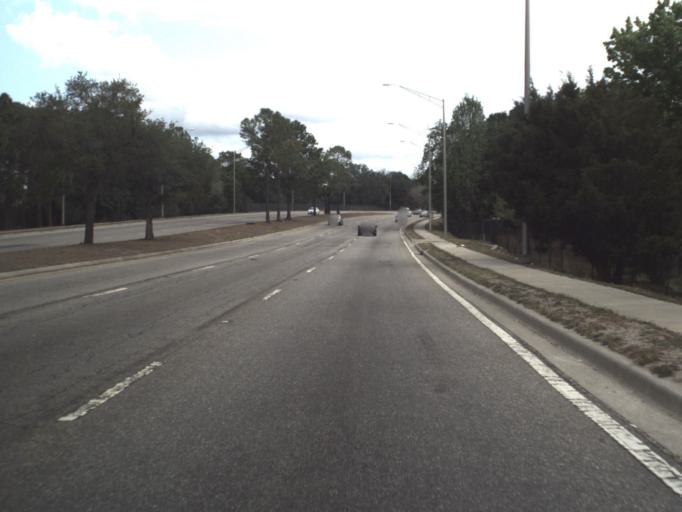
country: US
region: Florida
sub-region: Orange County
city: Holden Heights
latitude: 28.5220
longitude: -81.4174
